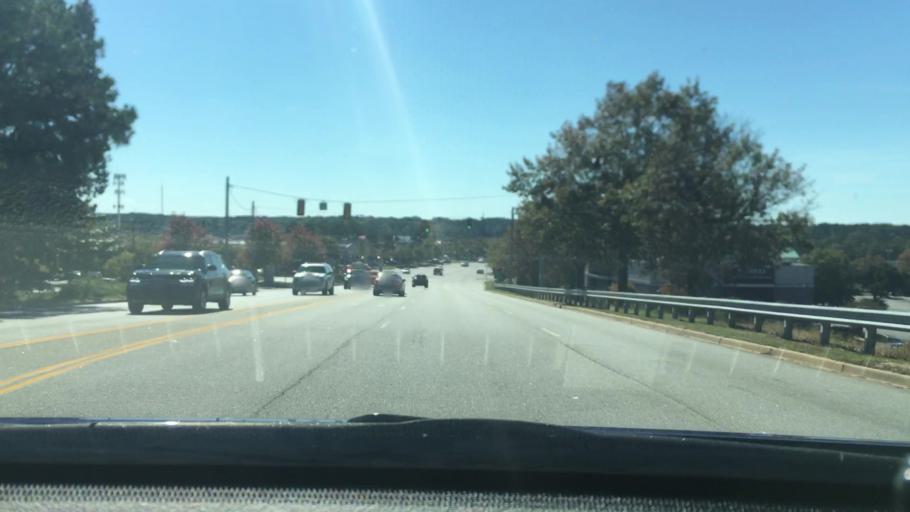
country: US
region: South Carolina
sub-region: Lexington County
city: Seven Oaks
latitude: 34.0764
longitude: -81.1540
